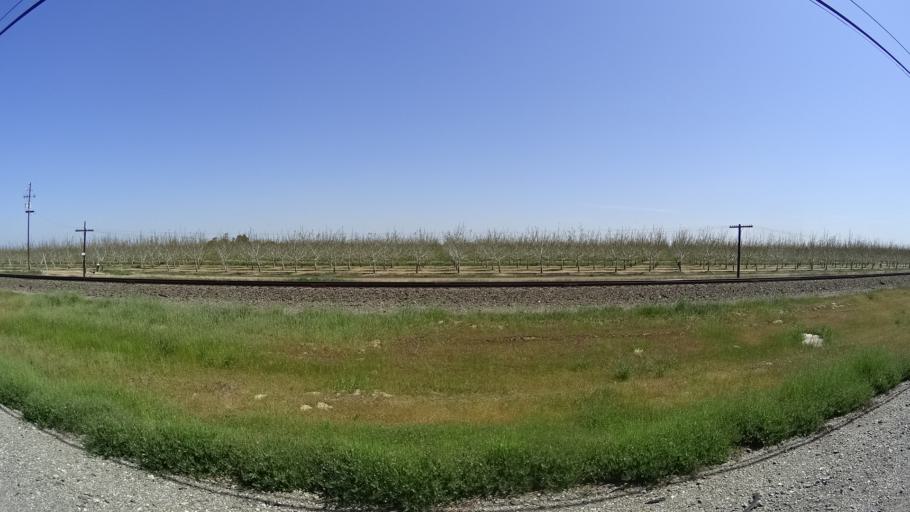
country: US
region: California
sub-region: Glenn County
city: Willows
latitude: 39.6089
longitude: -122.1940
